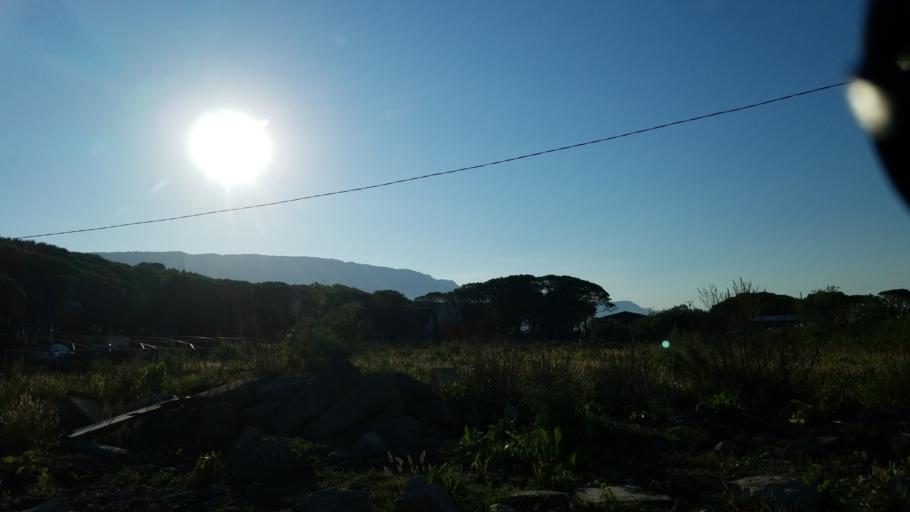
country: AL
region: Shkoder
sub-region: Rrethi i Shkodres
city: Velipoje
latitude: 41.8613
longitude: 19.4358
